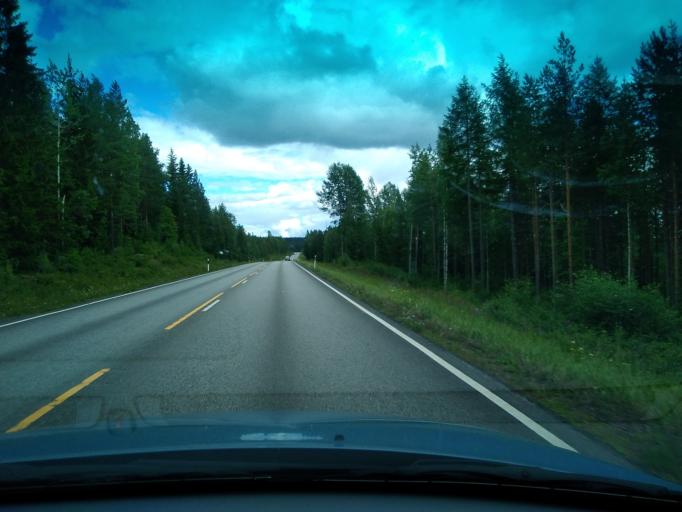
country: FI
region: Central Finland
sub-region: Saarijaervi-Viitasaari
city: Saarijaervi
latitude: 62.7209
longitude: 25.2063
